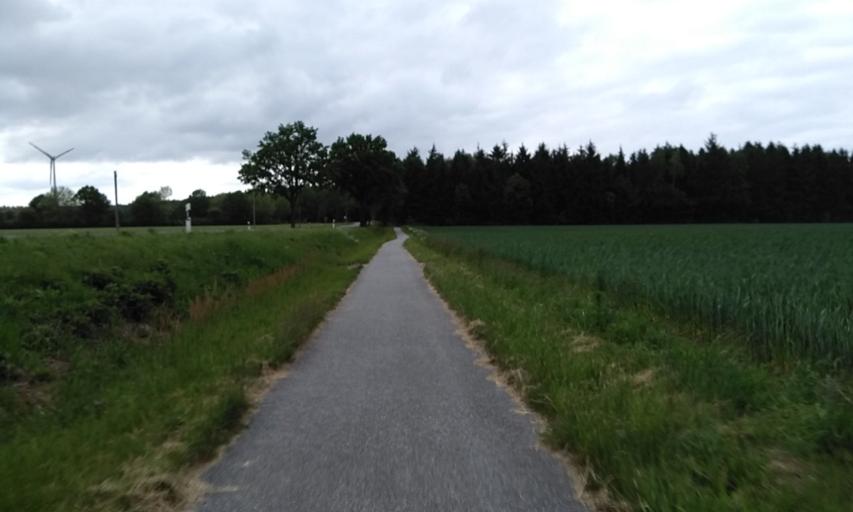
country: DE
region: Lower Saxony
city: Harsefeld
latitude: 53.4905
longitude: 9.4927
